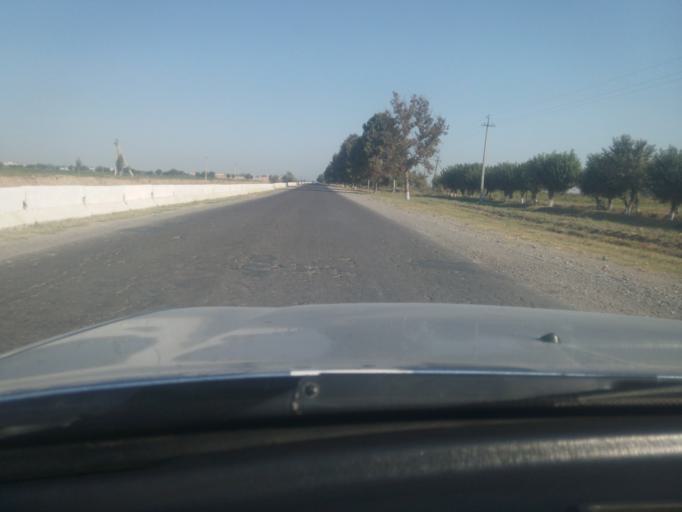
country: UZ
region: Sirdaryo
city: Guliston
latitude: 40.5006
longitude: 68.7984
